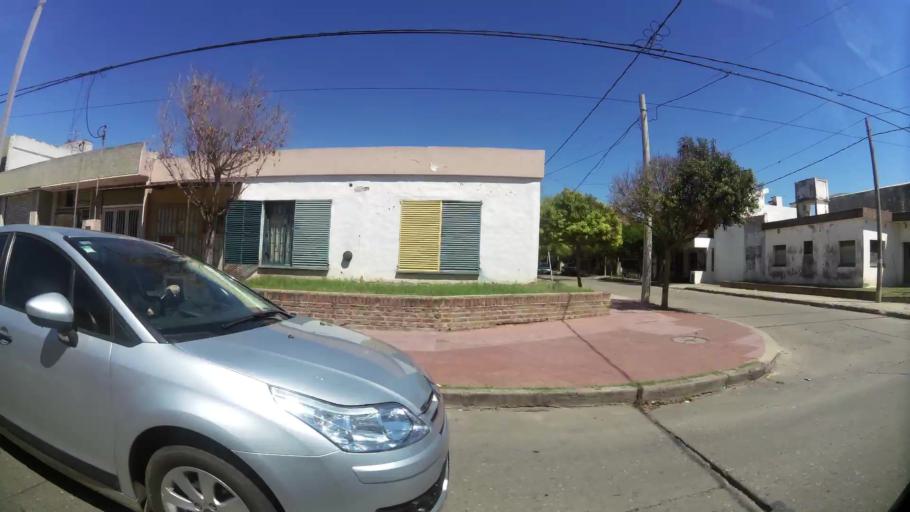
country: AR
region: Cordoba
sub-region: Departamento de Capital
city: Cordoba
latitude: -31.4235
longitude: -64.2094
